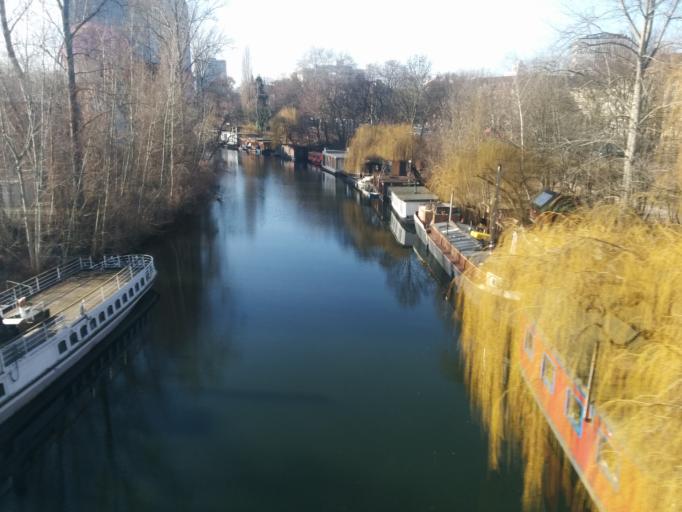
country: DE
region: Berlin
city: Hansaviertel
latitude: 52.5128
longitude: 13.3355
